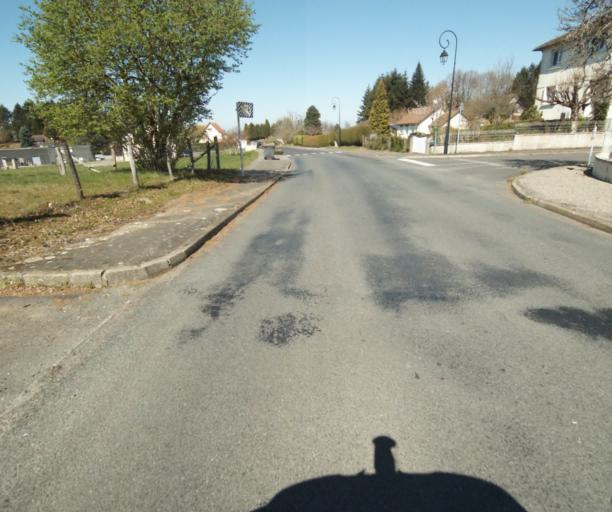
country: FR
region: Limousin
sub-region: Departement de la Correze
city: Saint-Mexant
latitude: 45.2790
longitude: 1.6610
